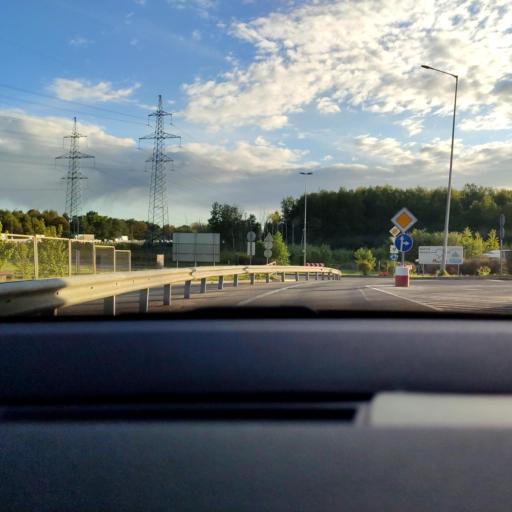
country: RU
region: Moscow
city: Lianozovo
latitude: 55.9121
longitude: 37.5707
